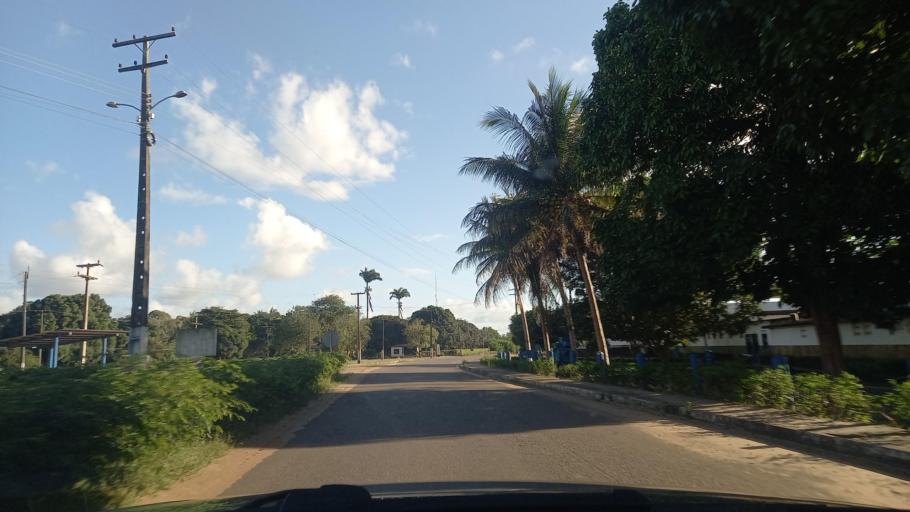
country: BR
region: Alagoas
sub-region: Sao Miguel Dos Campos
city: Sao Miguel dos Campos
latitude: -9.8073
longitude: -36.2097
